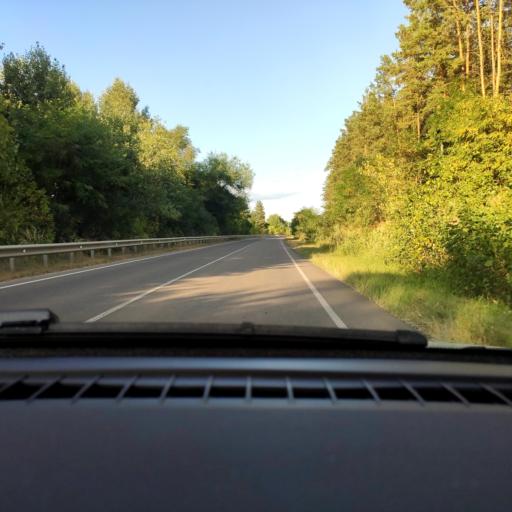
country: RU
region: Voronezj
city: Semiluki
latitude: 51.6726
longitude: 39.0250
